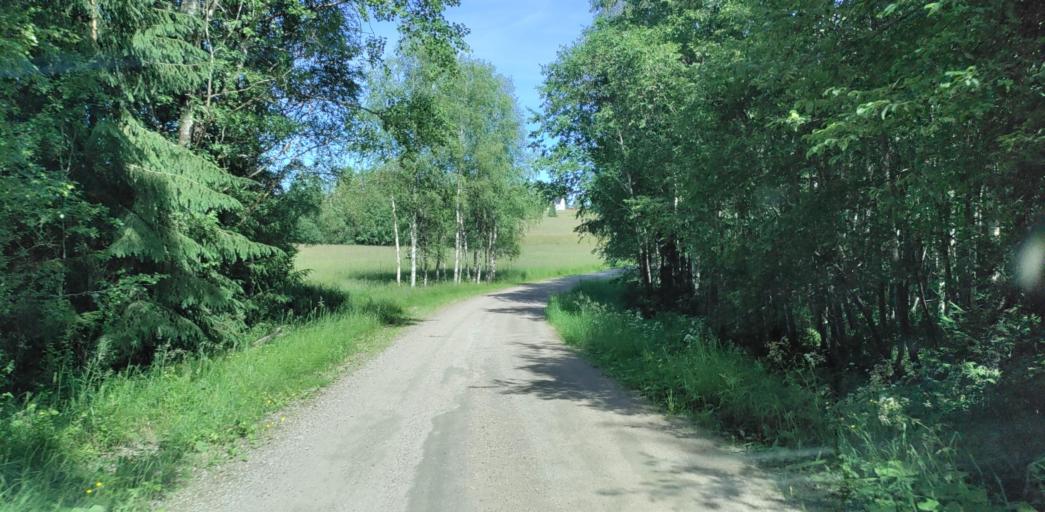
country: SE
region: Vaermland
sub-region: Hagfors Kommun
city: Ekshaerad
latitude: 60.1010
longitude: 13.4448
